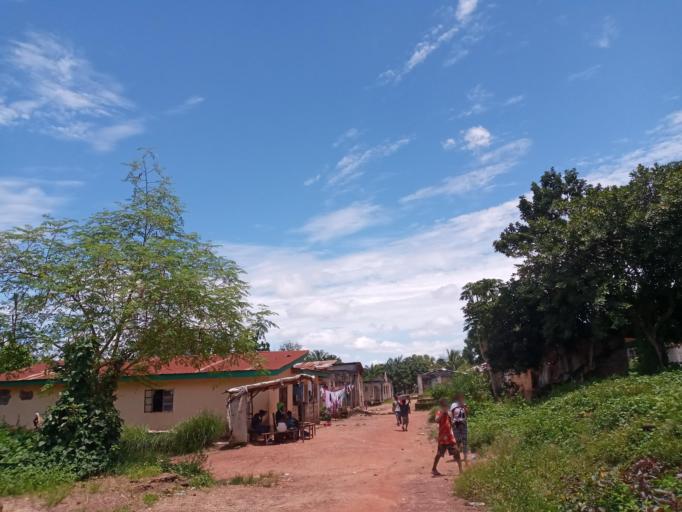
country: SL
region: Eastern Province
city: Koidu
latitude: 8.6488
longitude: -10.9609
